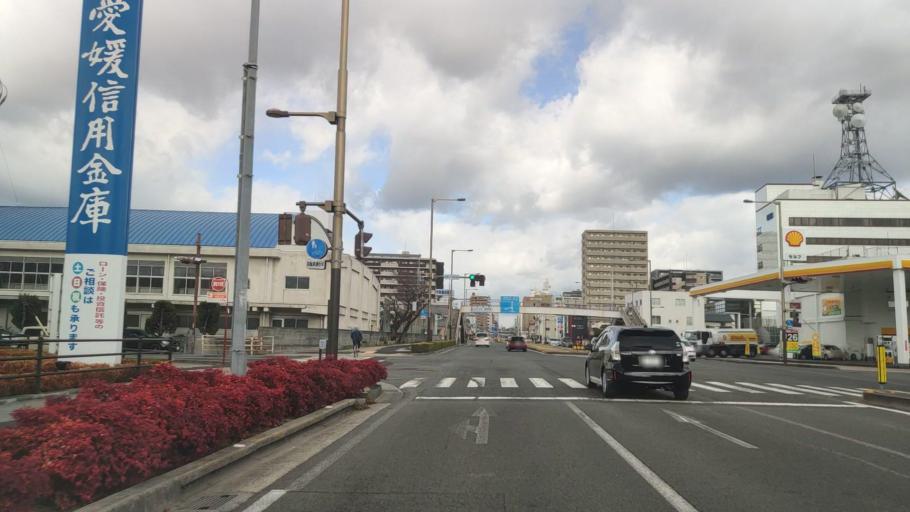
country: JP
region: Ehime
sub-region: Shikoku-chuo Shi
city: Matsuyama
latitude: 33.8310
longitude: 132.7588
